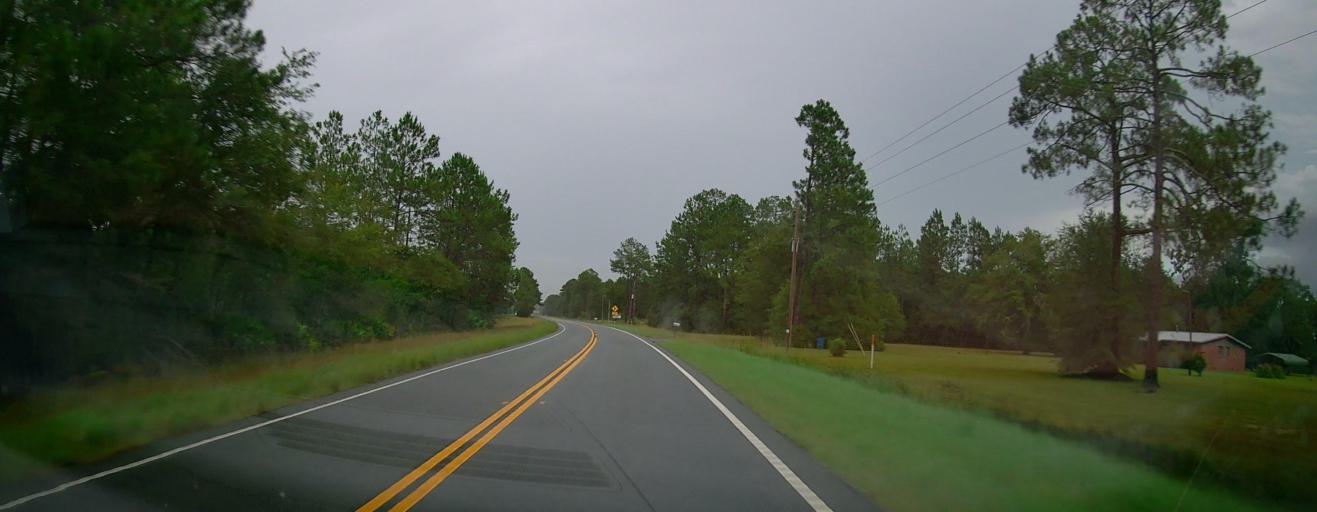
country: US
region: Georgia
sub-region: Brantley County
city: Nahunta
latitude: 31.3307
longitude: -81.9256
